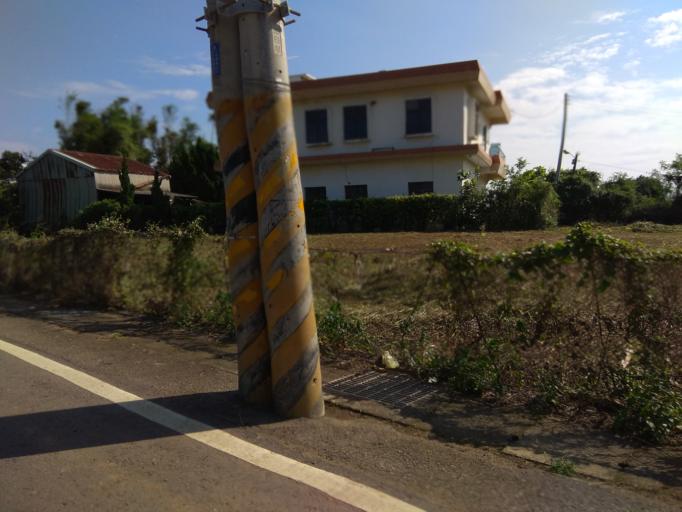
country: TW
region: Taiwan
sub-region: Hsinchu
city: Zhubei
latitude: 24.9464
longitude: 121.0006
